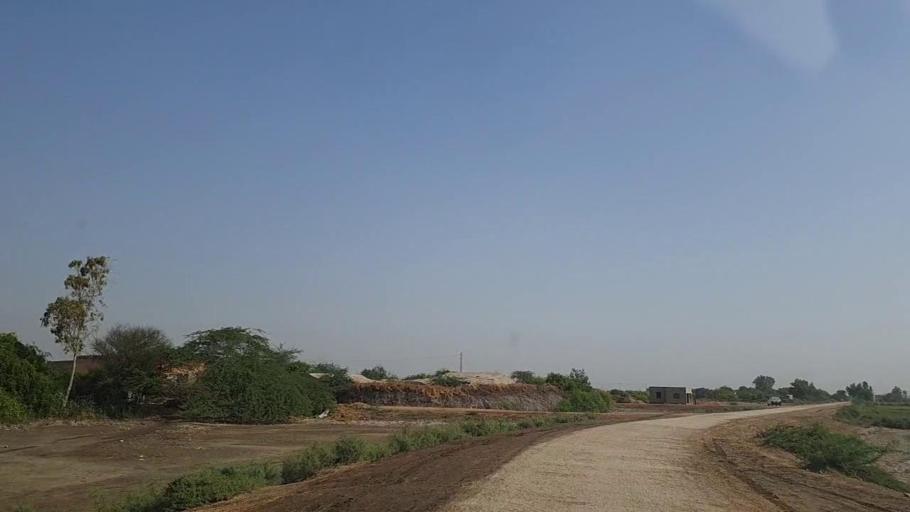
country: PK
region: Sindh
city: Thatta
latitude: 24.6862
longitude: 68.0481
